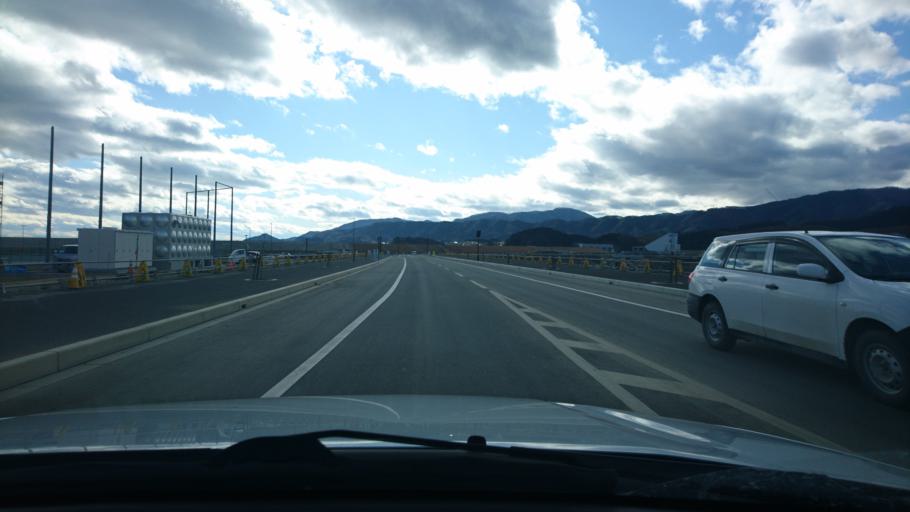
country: JP
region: Iwate
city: Ofunato
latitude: 39.0118
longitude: 141.6325
